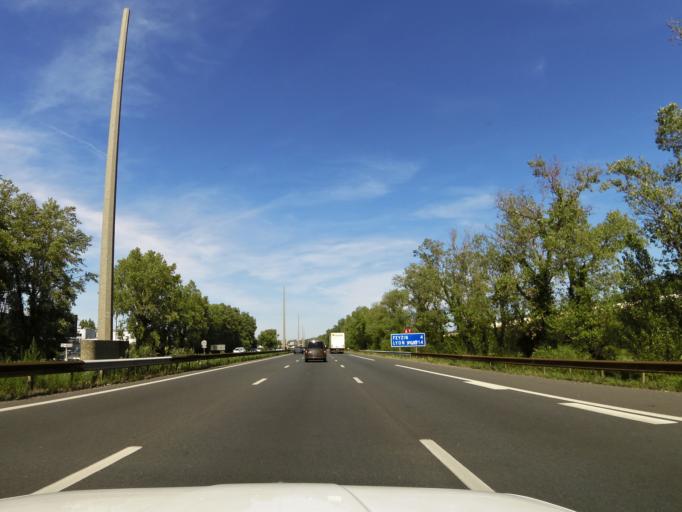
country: FR
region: Rhone-Alpes
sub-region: Departement du Rhone
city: Serezin-du-Rhone
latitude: 45.6460
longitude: 4.8316
